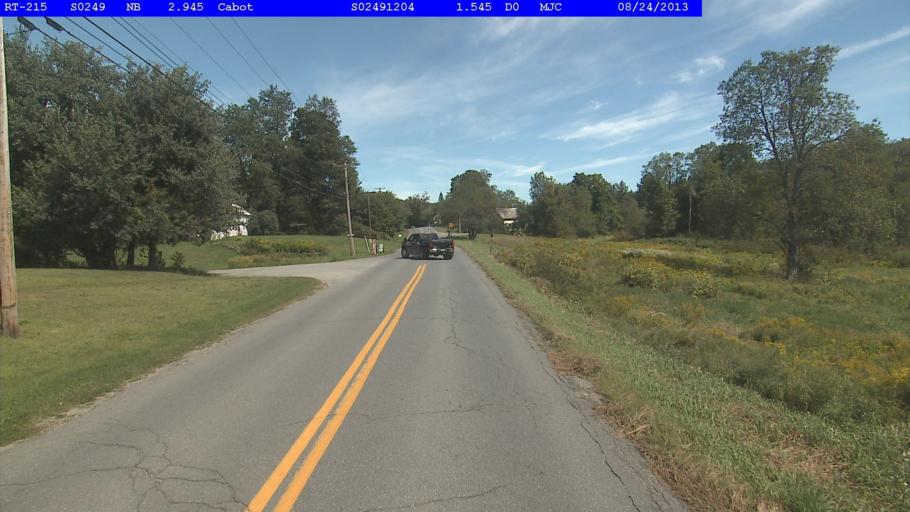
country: US
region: Vermont
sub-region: Caledonia County
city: Hardwick
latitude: 44.3892
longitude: -72.3330
